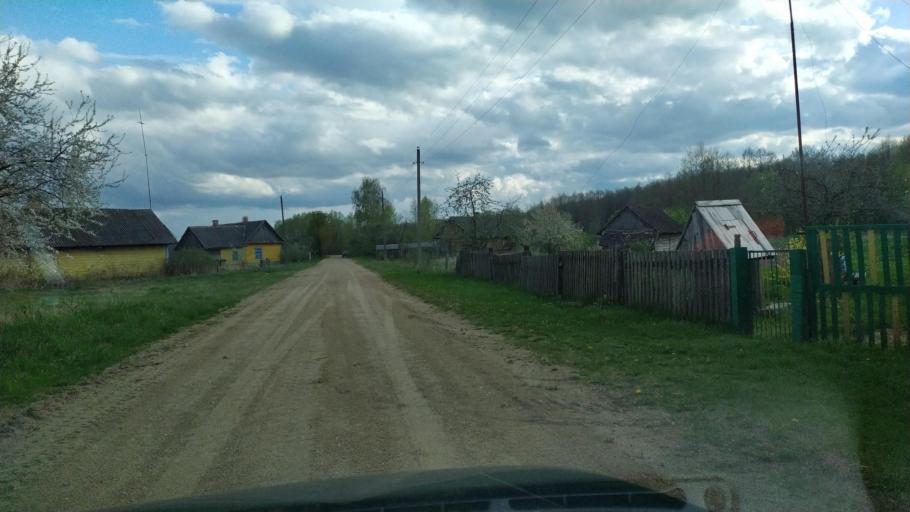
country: BY
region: Brest
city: Pruzhany
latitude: 52.7101
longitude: 24.2595
